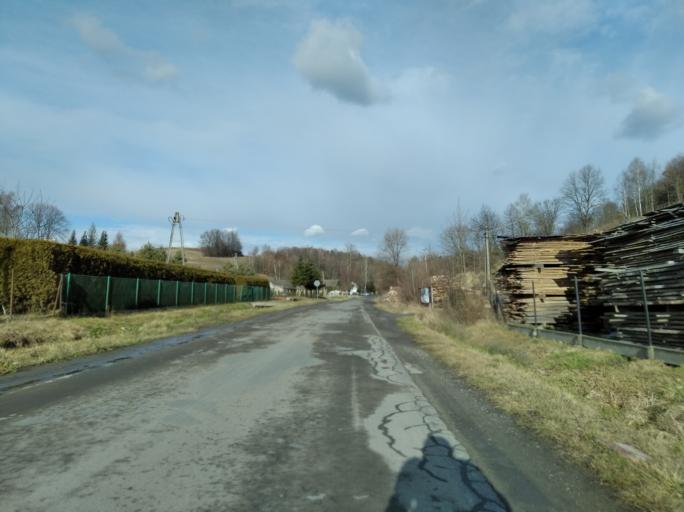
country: PL
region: Subcarpathian Voivodeship
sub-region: Powiat strzyzowski
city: Strzyzow
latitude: 49.8889
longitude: 21.7552
